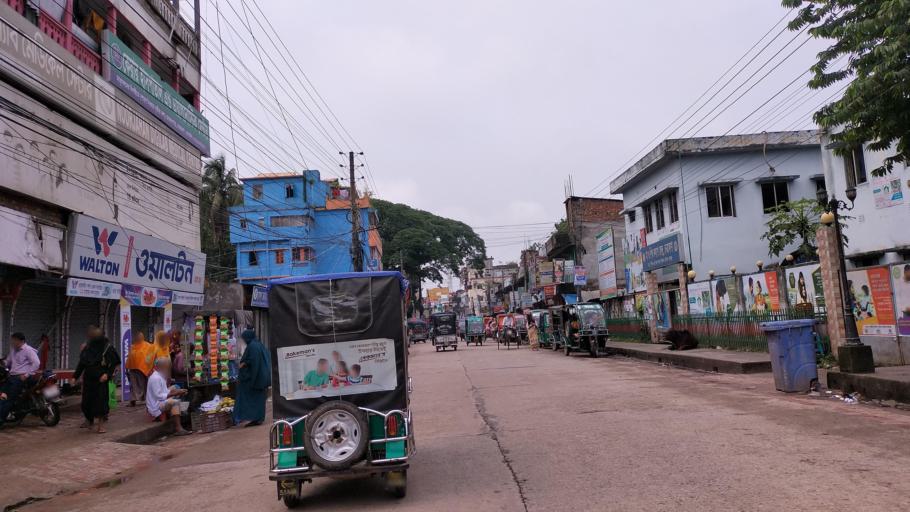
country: BD
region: Dhaka
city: Netrakona
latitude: 24.8795
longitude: 90.7313
